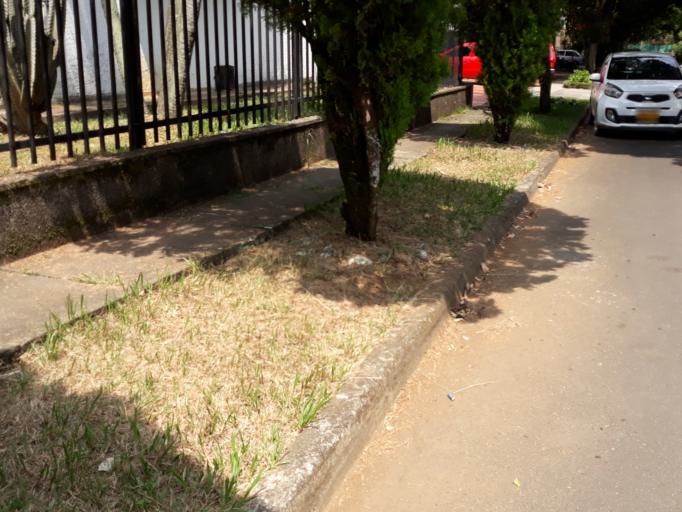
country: CO
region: Valle del Cauca
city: Cali
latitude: 3.3785
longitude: -76.5416
